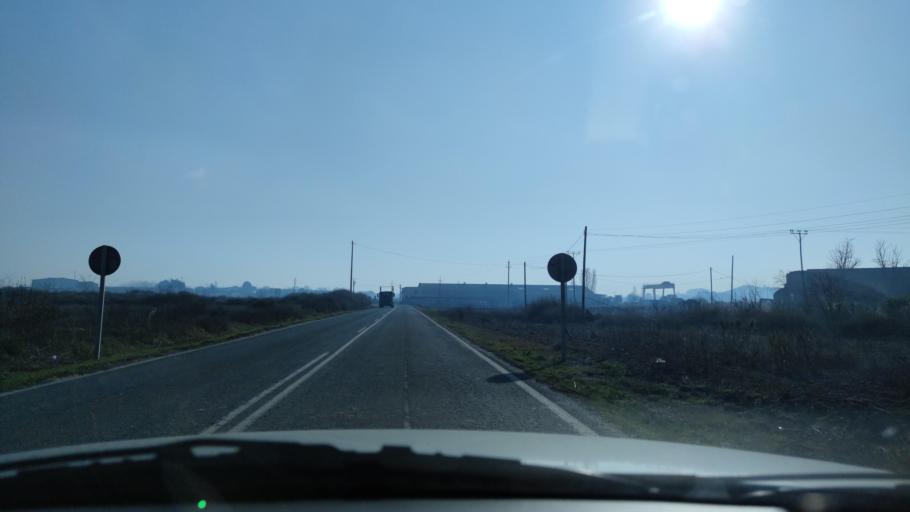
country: ES
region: Catalonia
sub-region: Provincia de Lleida
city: Alcoletge
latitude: 41.6242
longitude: 0.7223
